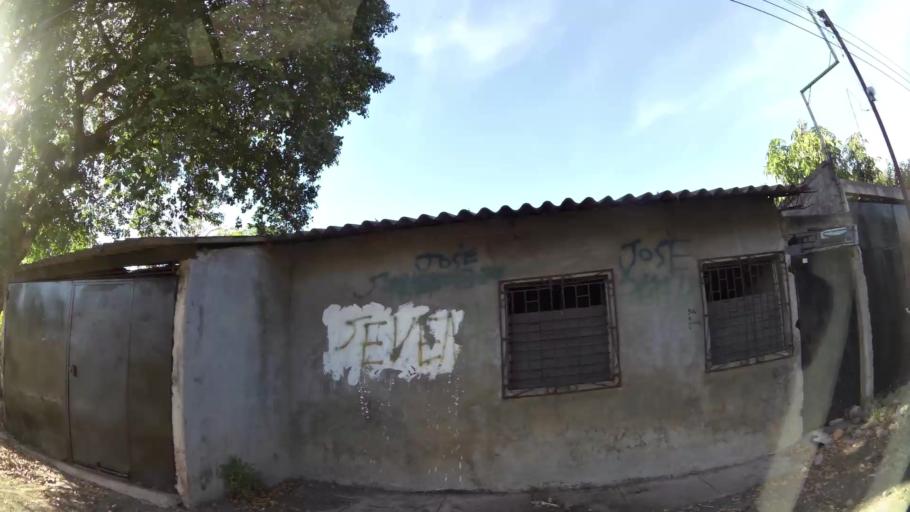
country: SV
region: San Miguel
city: San Miguel
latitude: 13.4675
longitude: -88.1873
